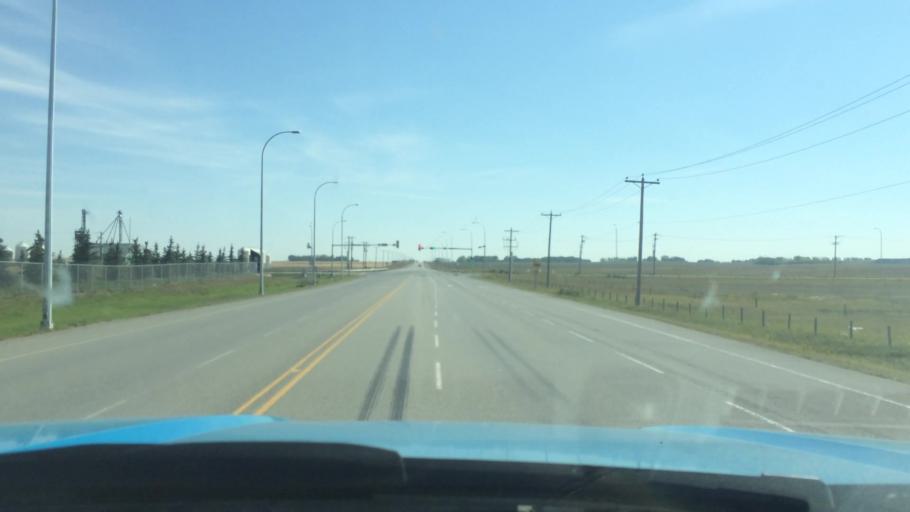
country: CA
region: Alberta
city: Airdrie
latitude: 51.2126
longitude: -113.9382
